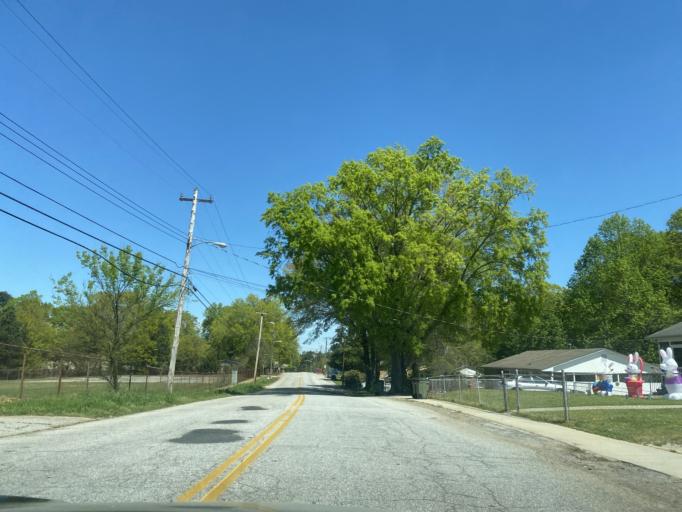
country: US
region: South Carolina
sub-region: Cherokee County
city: Gaffney
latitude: 35.0665
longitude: -81.6388
